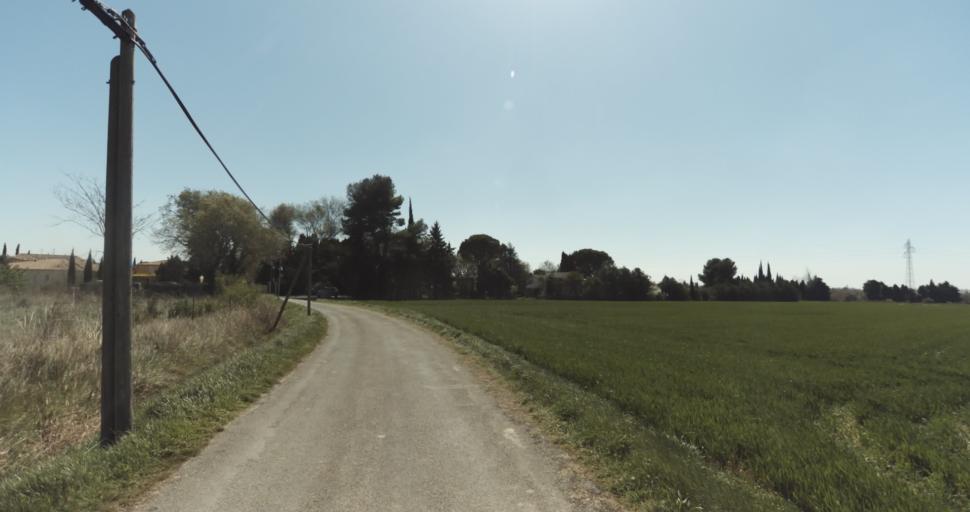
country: FR
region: Provence-Alpes-Cote d'Azur
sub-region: Departement des Bouches-du-Rhone
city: Pelissanne
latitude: 43.6343
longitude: 5.1792
